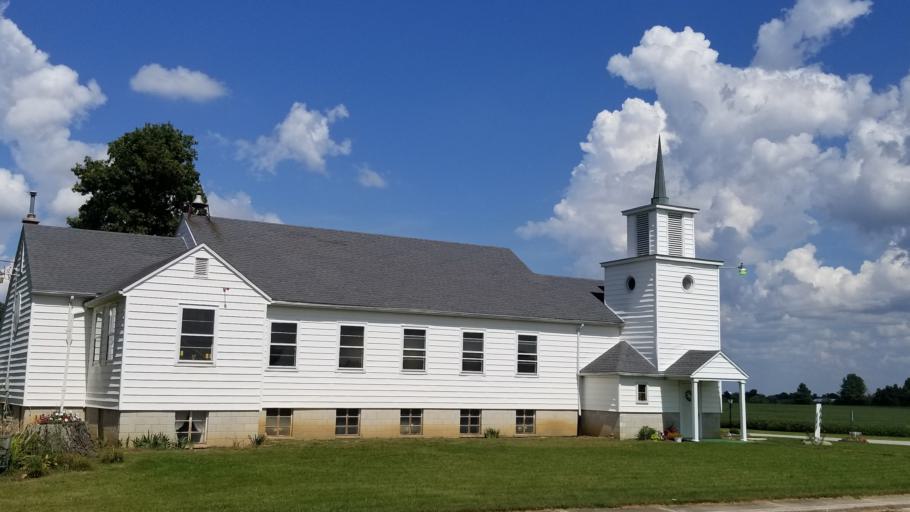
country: US
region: Ohio
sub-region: Hancock County
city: Arlington
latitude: 40.8627
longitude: -83.6004
